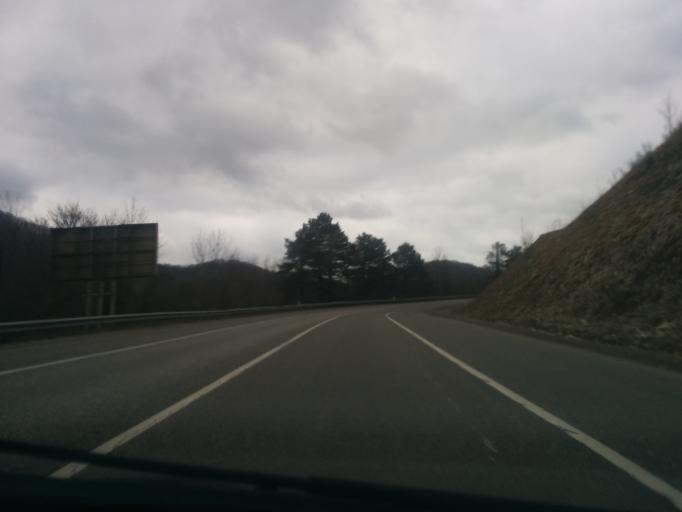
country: RU
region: Krasnodarskiy
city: Novomikhaylovskiy
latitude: 44.2571
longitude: 38.8824
